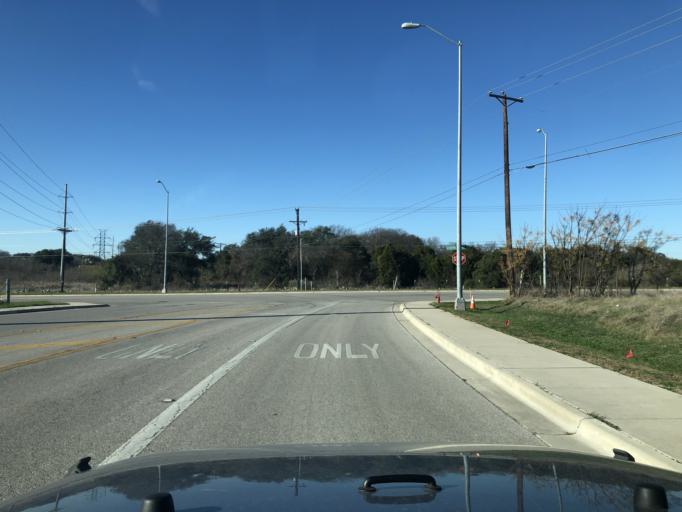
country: US
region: Texas
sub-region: Williamson County
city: Round Rock
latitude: 30.5274
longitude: -97.6939
